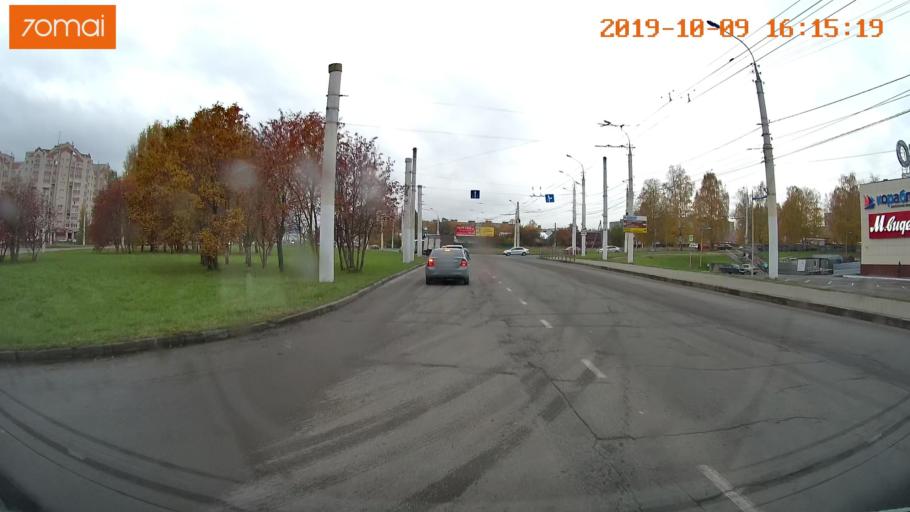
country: RU
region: Kostroma
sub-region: Kostromskoy Rayon
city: Kostroma
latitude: 57.7405
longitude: 40.9169
